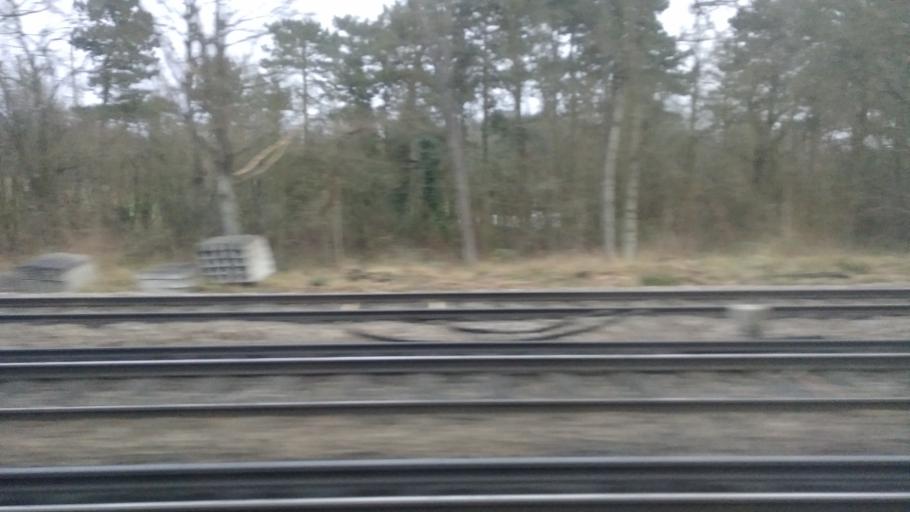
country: GB
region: England
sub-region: Greater London
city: Chislehurst
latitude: 51.4017
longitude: 0.0615
